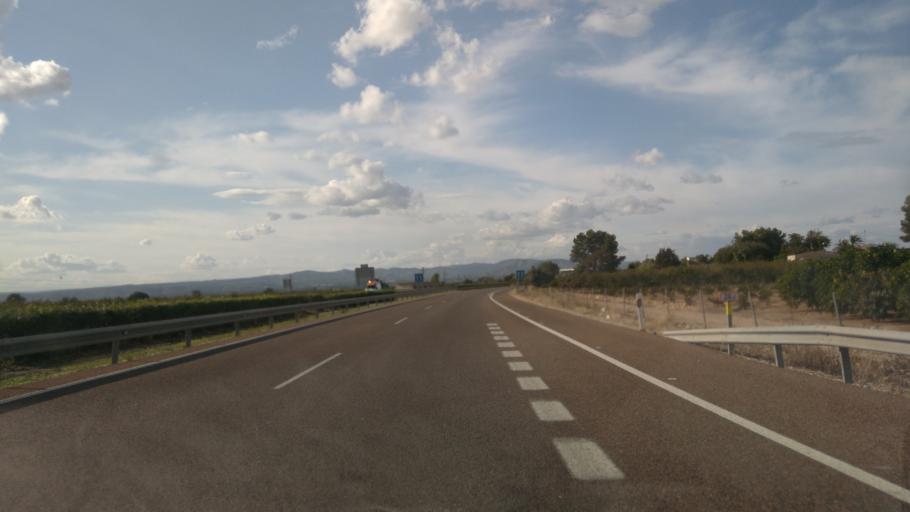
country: ES
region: Valencia
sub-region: Provincia de Valencia
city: Guadassuar
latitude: 39.1782
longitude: -0.4812
